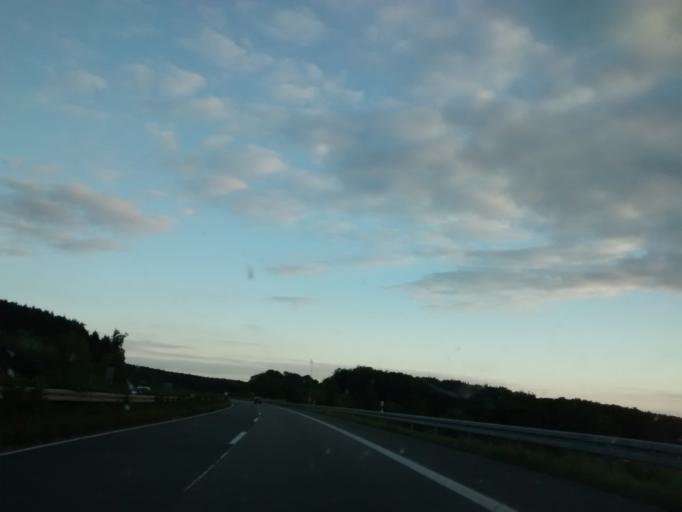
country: DE
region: Lower Saxony
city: Hilter
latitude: 52.1449
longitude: 8.1569
